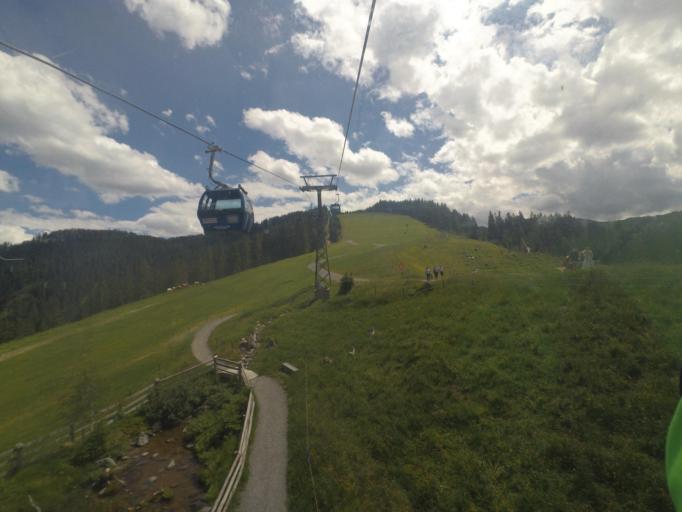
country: AT
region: Salzburg
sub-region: Politischer Bezirk Zell am See
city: Leogang
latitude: 47.4257
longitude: 12.7139
